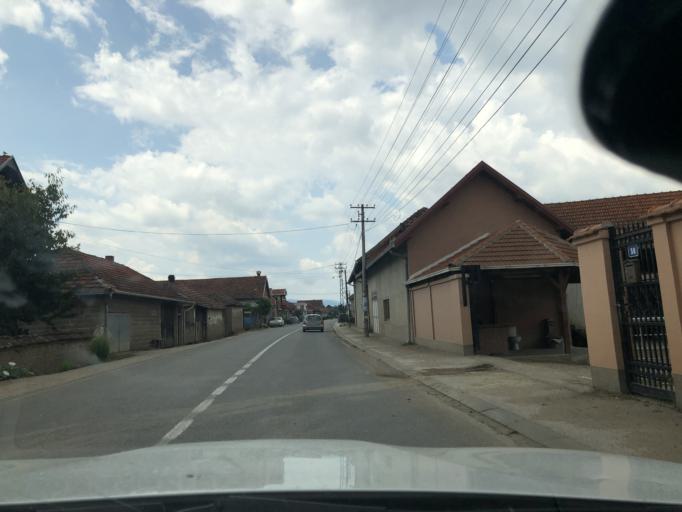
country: RS
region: Central Serbia
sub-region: Jablanicki Okrug
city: Lebane
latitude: 42.9463
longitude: 21.8251
